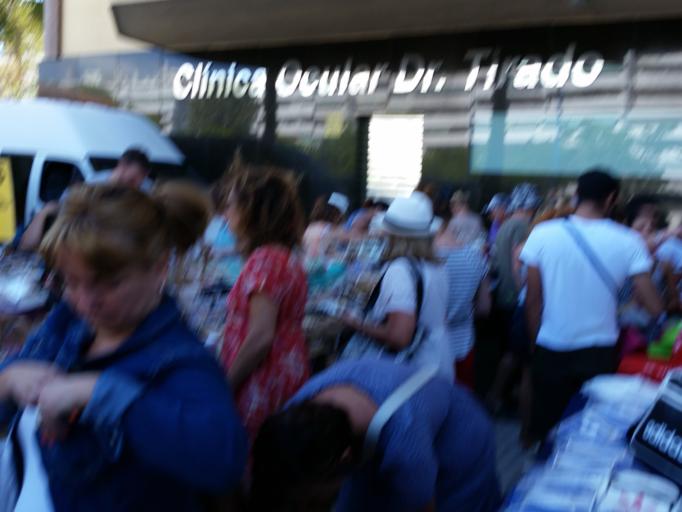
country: ES
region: Andalusia
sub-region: Provincia de Malaga
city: Fuengirola
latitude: 36.5294
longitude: -4.6271
